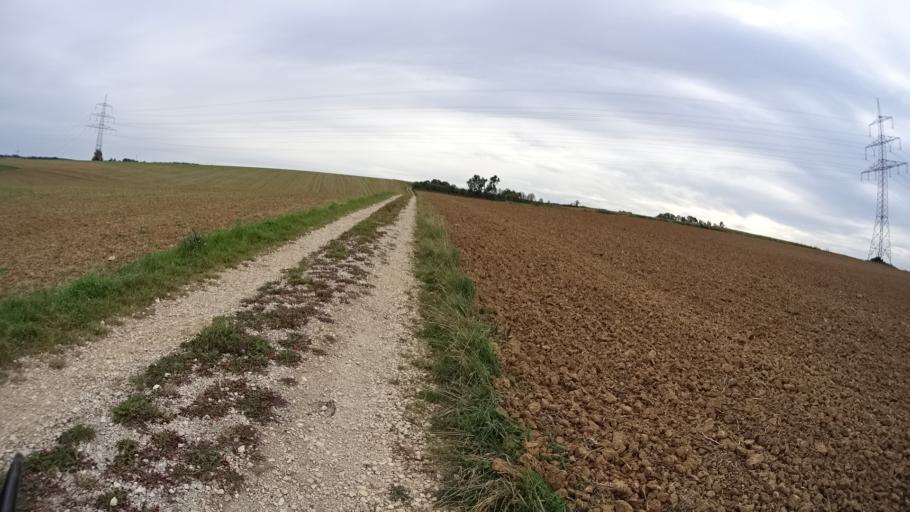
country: DE
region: Bavaria
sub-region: Upper Bavaria
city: Hitzhofen
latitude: 48.8664
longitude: 11.3367
